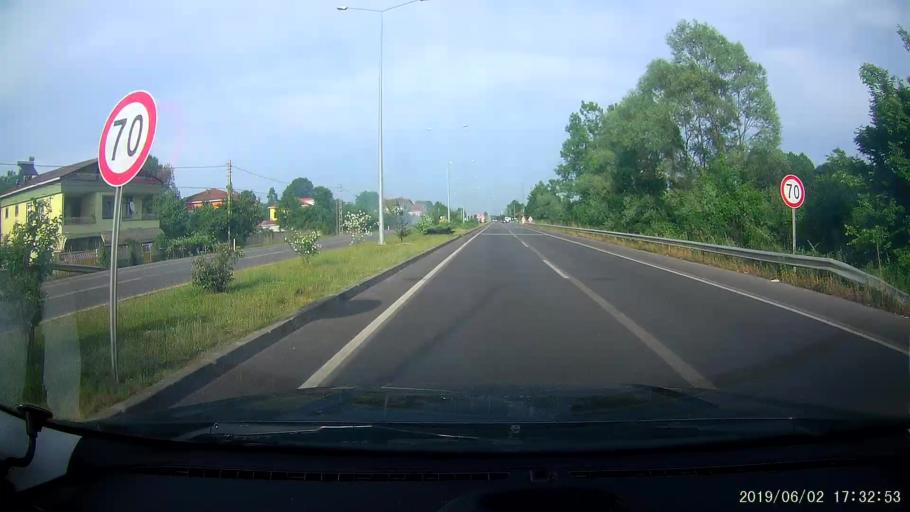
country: TR
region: Samsun
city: Carsamba
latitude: 41.2205
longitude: 36.8368
